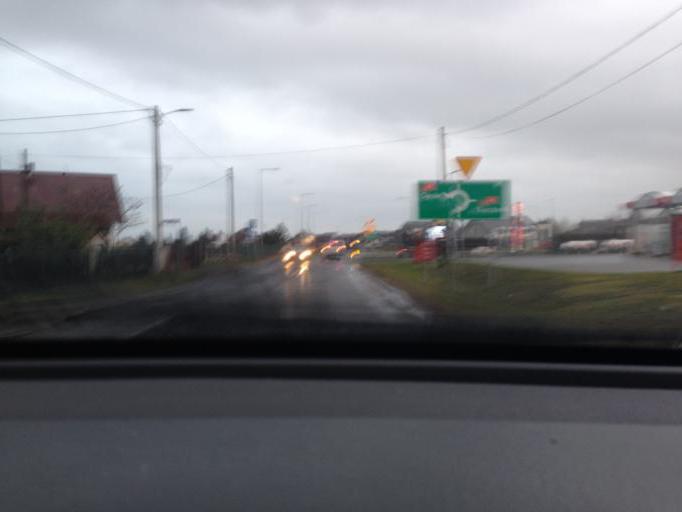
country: PL
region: Opole Voivodeship
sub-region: Powiat opolski
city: Wegry
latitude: 50.7193
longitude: 18.0040
